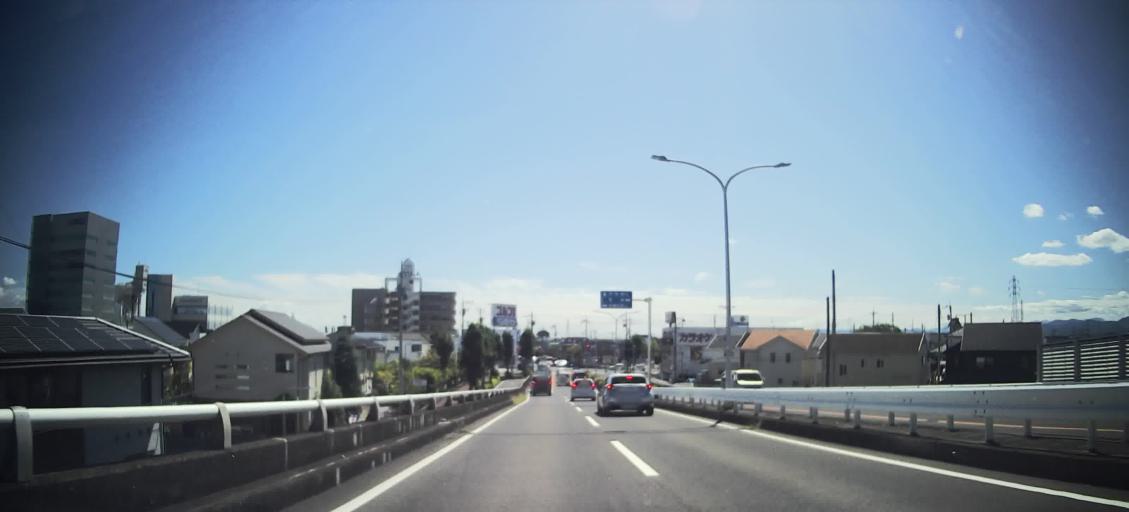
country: JP
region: Gunma
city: Maebashi-shi
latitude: 36.3758
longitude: 139.0428
